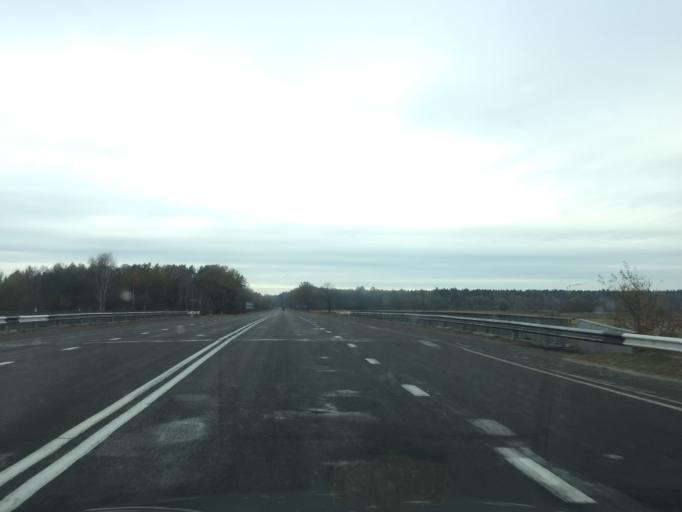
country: BY
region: Gomel
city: Gomel
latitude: 52.3920
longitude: 30.8283
